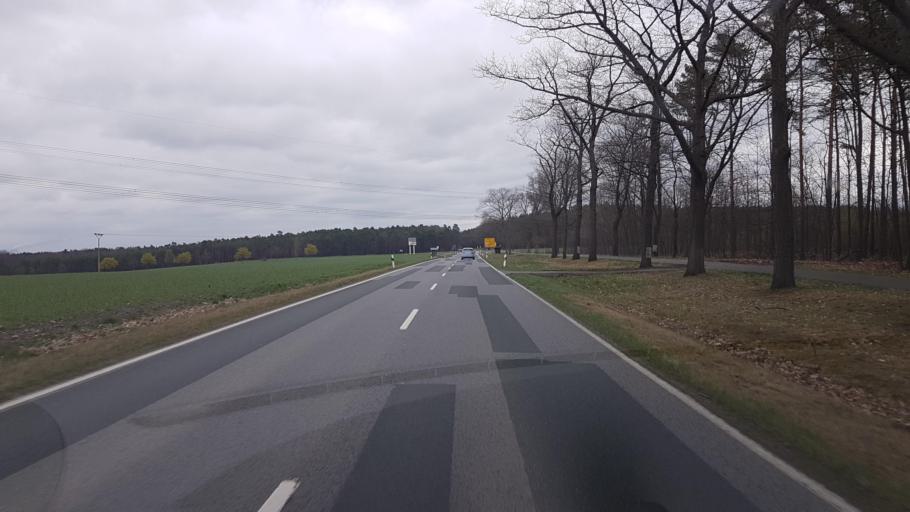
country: DE
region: Saxony
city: Ossling
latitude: 51.3702
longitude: 14.1879
